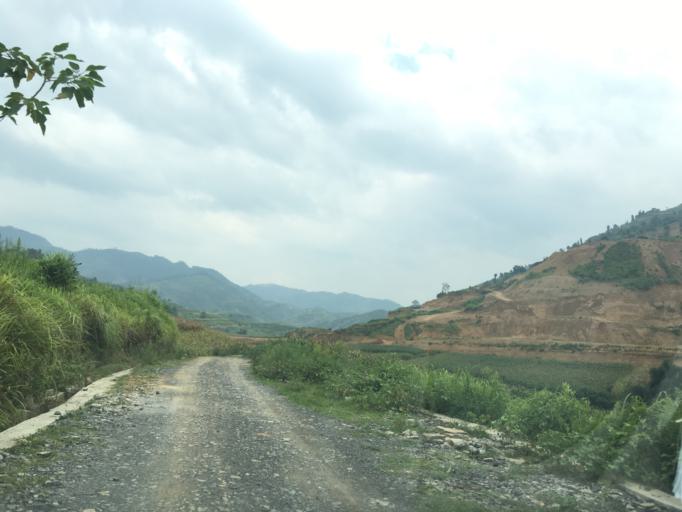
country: CN
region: Guangxi Zhuangzu Zizhiqu
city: Xinzhou
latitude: 25.1870
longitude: 105.7324
